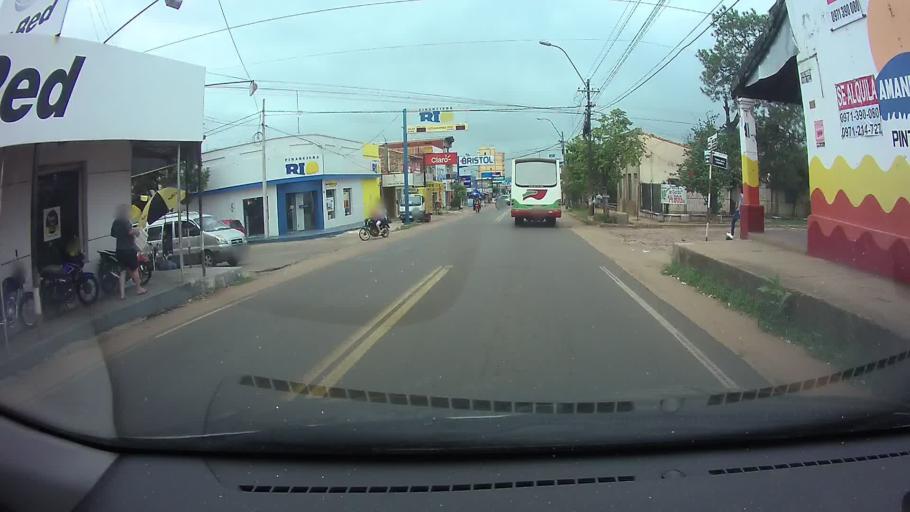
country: PY
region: Paraguari
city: Carapegua
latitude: -25.7684
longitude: -57.2416
